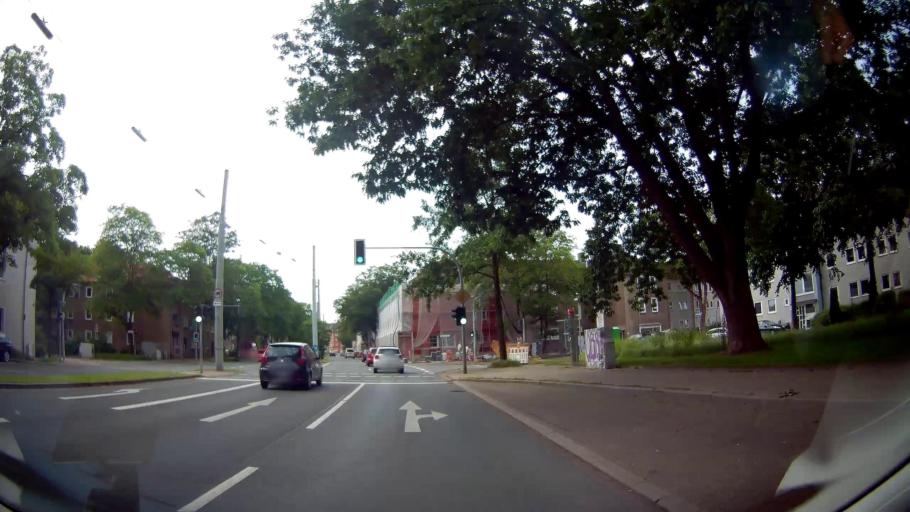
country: DE
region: North Rhine-Westphalia
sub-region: Regierungsbezirk Arnsberg
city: Herne
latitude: 51.5327
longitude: 7.2194
